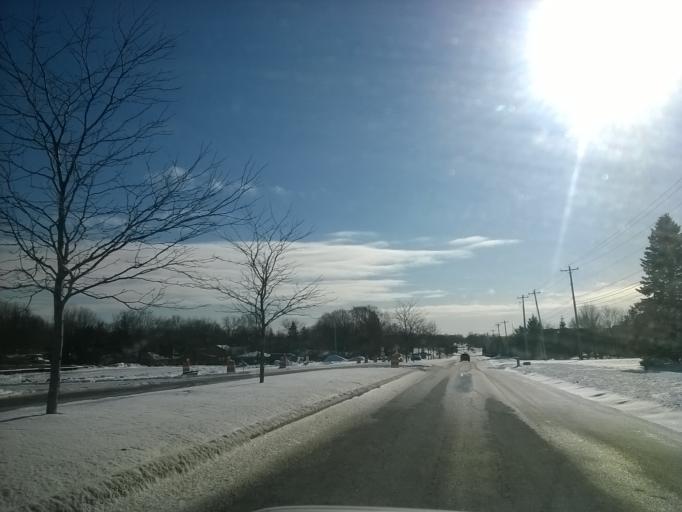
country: US
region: Indiana
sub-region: Hamilton County
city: Carmel
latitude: 39.9319
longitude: -86.1269
